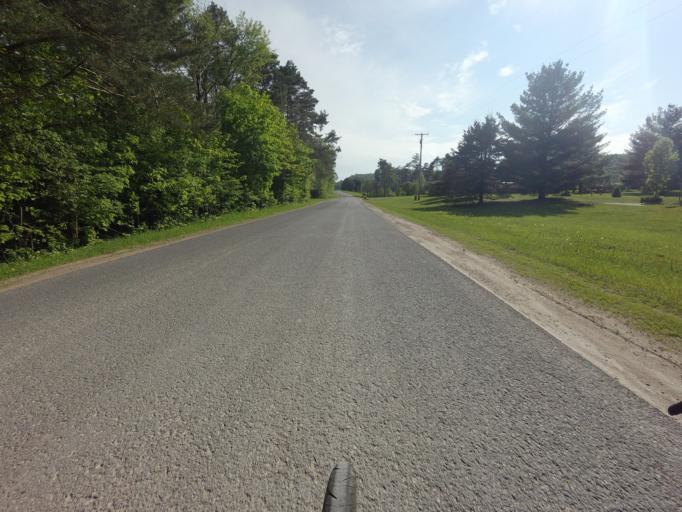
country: US
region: New York
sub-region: St. Lawrence County
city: Gouverneur
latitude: 44.2254
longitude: -75.2325
